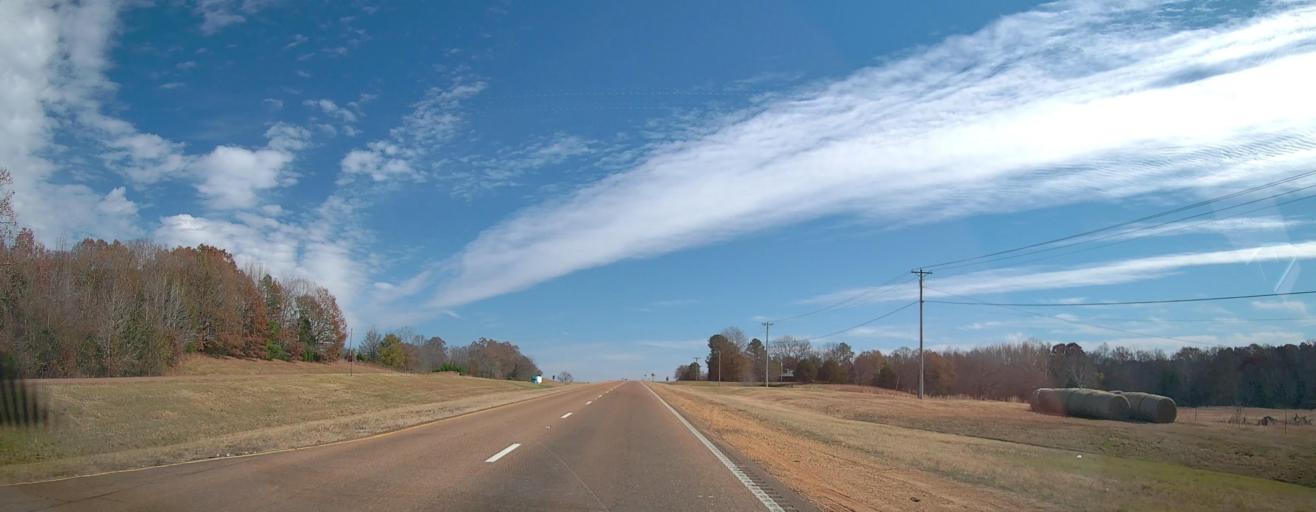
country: US
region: Mississippi
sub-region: Marshall County
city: Holly Springs
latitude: 34.9462
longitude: -89.3958
